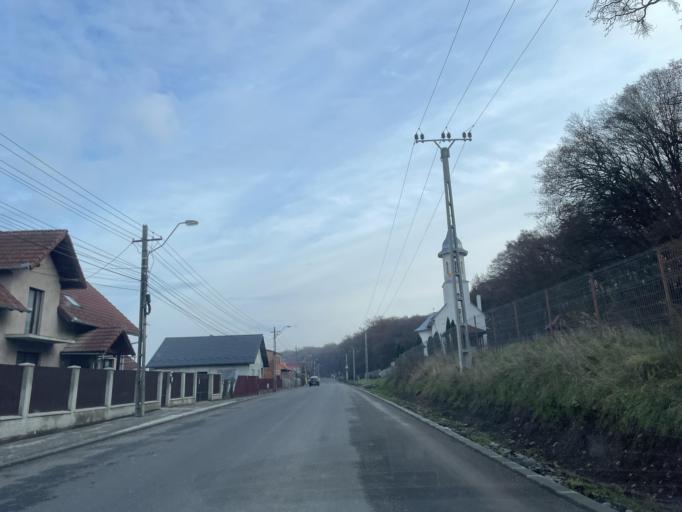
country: RO
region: Mures
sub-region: Comuna Ideciu de Jos
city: Ideciu de Jos
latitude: 46.7764
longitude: 24.7415
